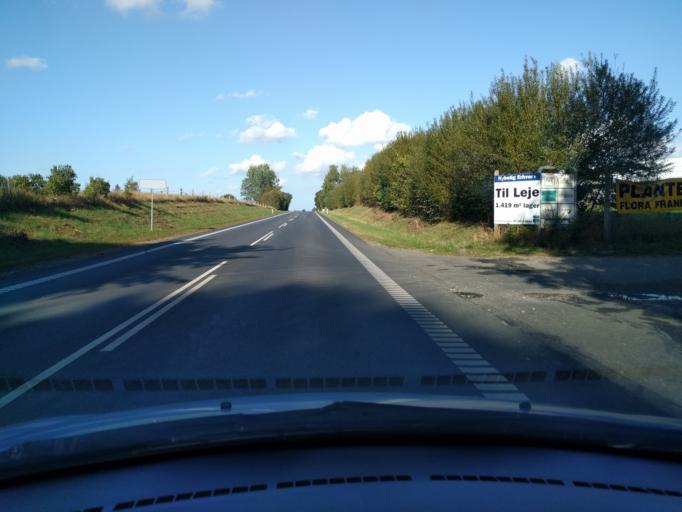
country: DK
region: South Denmark
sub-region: Assens Kommune
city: Tommerup
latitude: 55.3046
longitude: 10.2593
